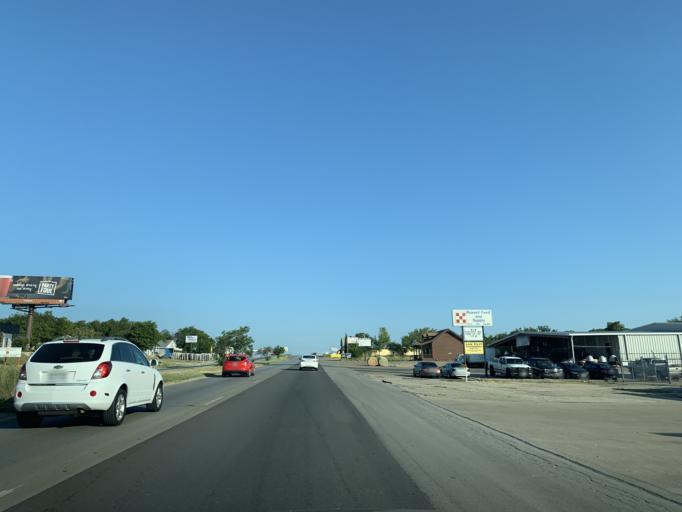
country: US
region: Texas
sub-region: Tarrant County
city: Sansom Park
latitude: 32.8013
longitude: -97.4083
